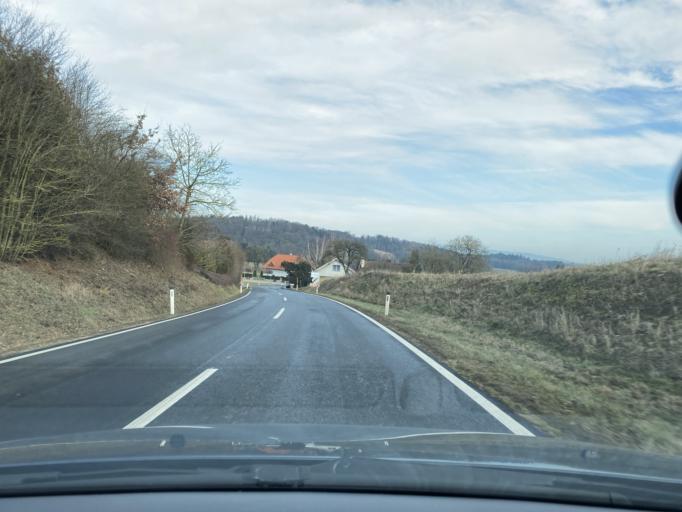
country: AT
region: Lower Austria
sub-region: Politischer Bezirk Melk
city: Loosdorf
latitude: 48.1678
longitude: 15.3509
